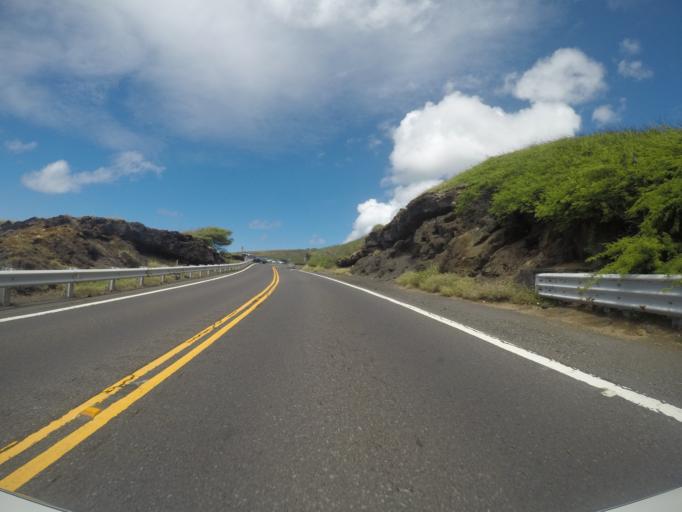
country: US
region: Hawaii
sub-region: Honolulu County
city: Waimanalo Beach
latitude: 21.2771
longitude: -157.6849
